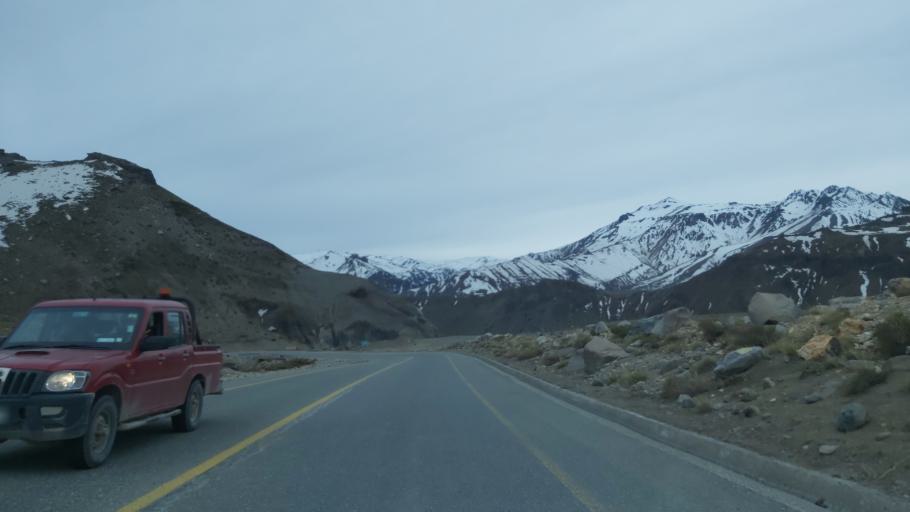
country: CL
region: Maule
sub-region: Provincia de Linares
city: Colbun
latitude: -35.9647
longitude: -70.5719
